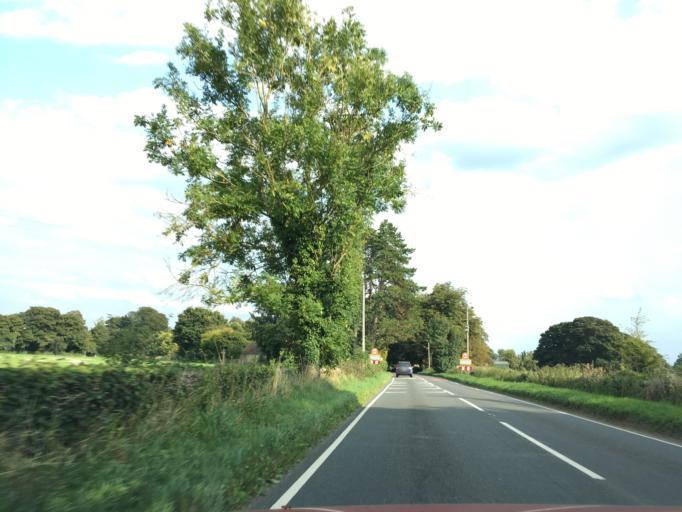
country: GB
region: England
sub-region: Gloucestershire
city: Tetbury
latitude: 51.6447
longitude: -2.2069
